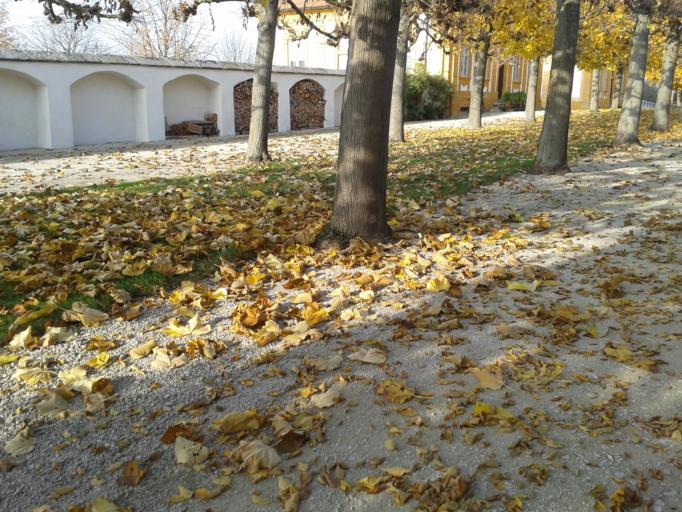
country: DE
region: Bavaria
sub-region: Upper Franconia
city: Memmelsdorf
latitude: 49.9275
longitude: 10.9437
